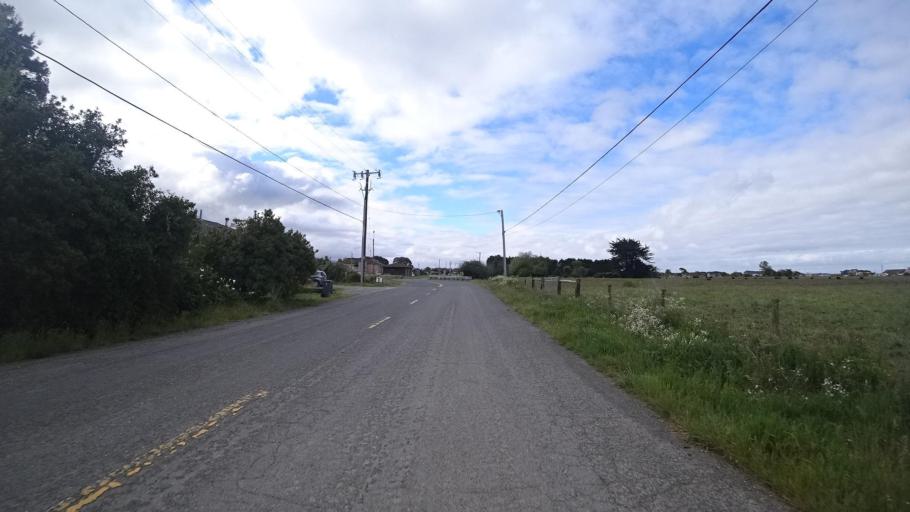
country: US
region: California
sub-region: Humboldt County
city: Arcata
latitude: 40.9042
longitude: -124.0914
